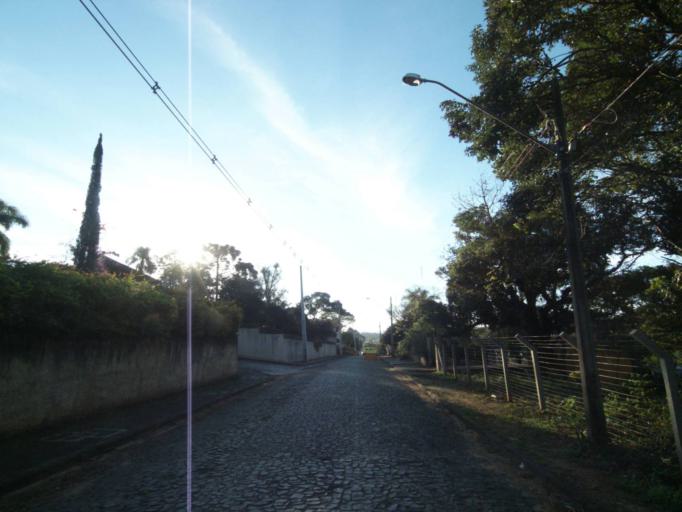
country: BR
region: Parana
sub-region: Tibagi
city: Tibagi
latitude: -24.5128
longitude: -50.4099
